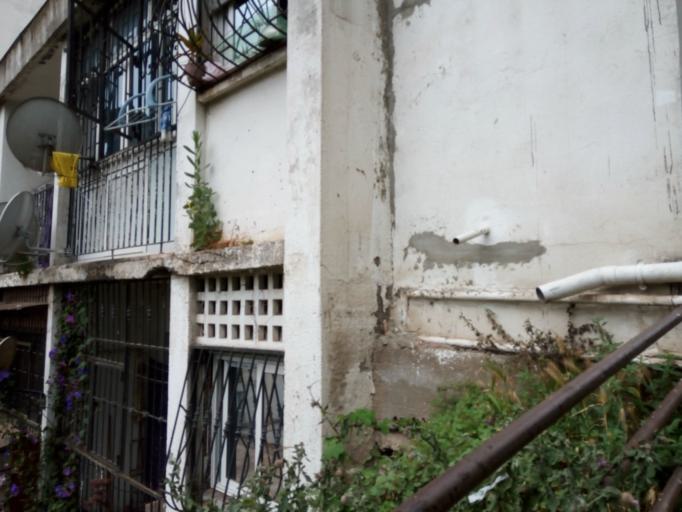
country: DZ
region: Alger
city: Algiers
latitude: 36.7654
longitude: 3.0386
